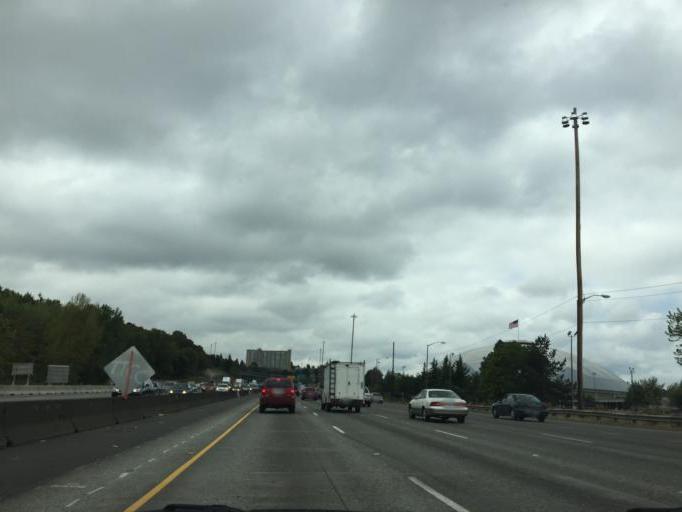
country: US
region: Washington
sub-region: Pierce County
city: Tacoma
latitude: 47.2374
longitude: -122.4209
